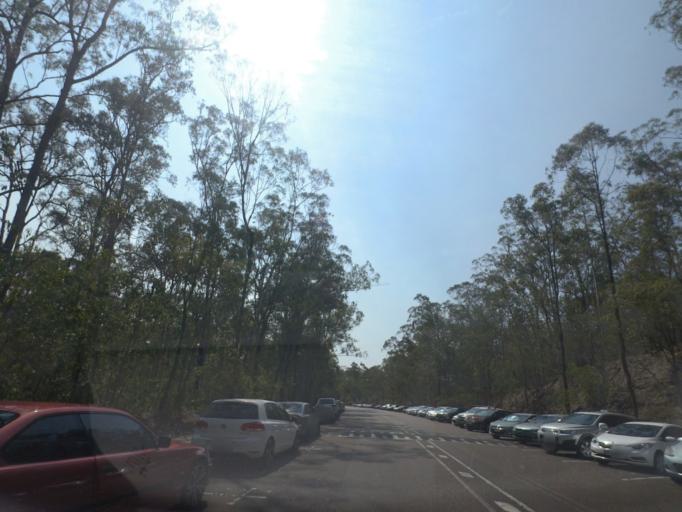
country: AU
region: Queensland
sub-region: Brisbane
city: Nathan
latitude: -27.5498
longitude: 153.0545
